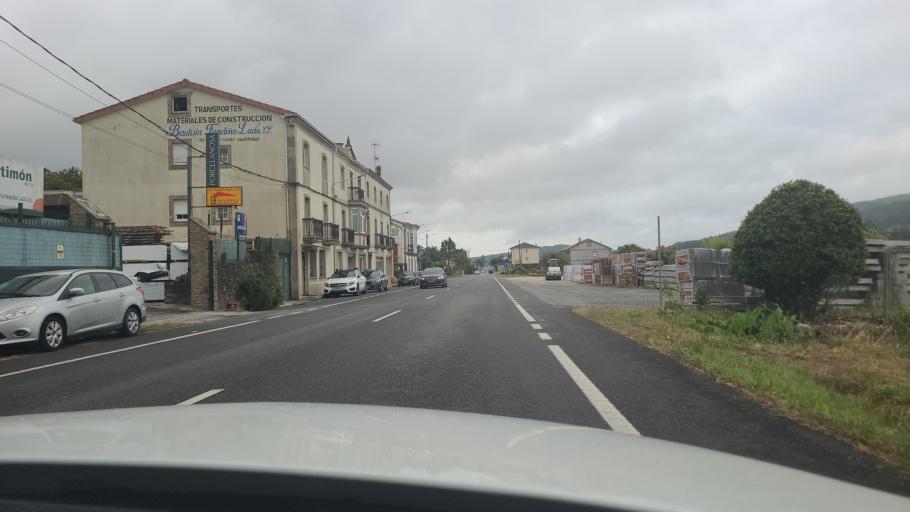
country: ES
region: Galicia
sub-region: Provincia da Coruna
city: Cee
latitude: 42.9898
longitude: -9.1837
